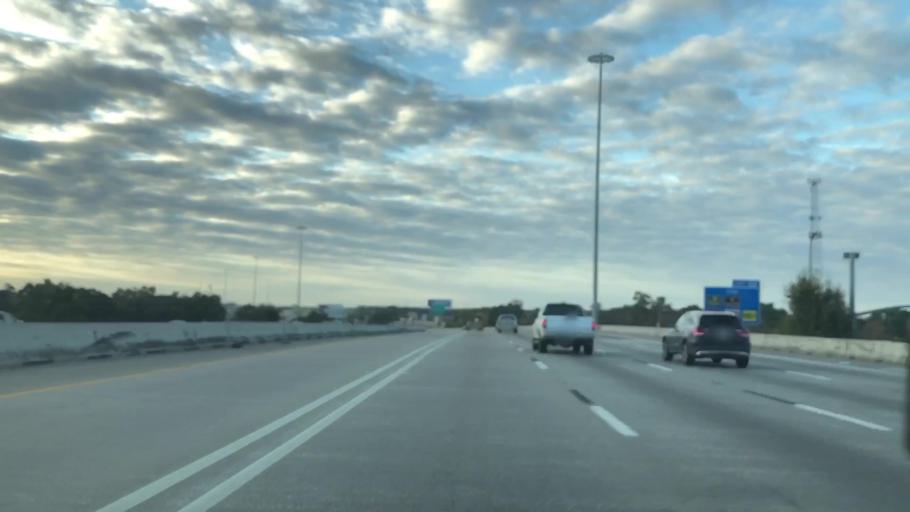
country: US
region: Texas
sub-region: Harris County
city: Spring
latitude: 30.0835
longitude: -95.4368
